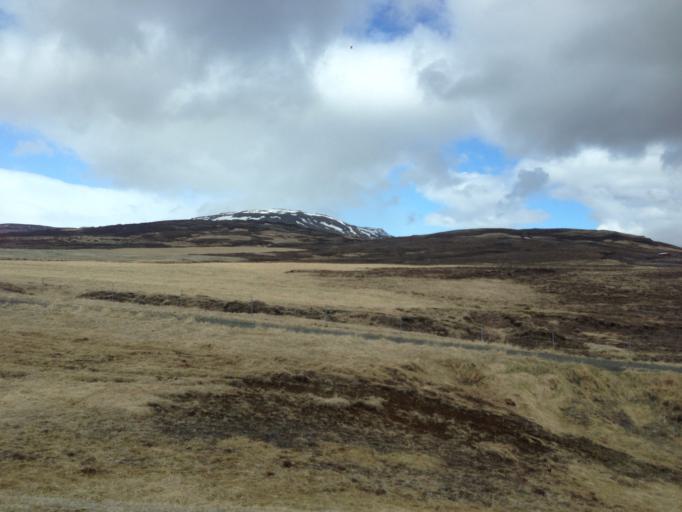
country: IS
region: South
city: Selfoss
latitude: 64.2759
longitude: -20.4110
